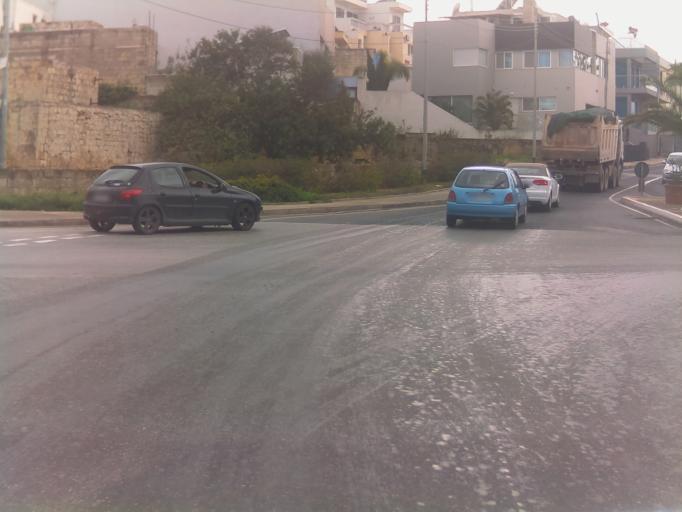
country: MT
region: Il-Mosta
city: Mosta
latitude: 35.9167
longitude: 14.4178
